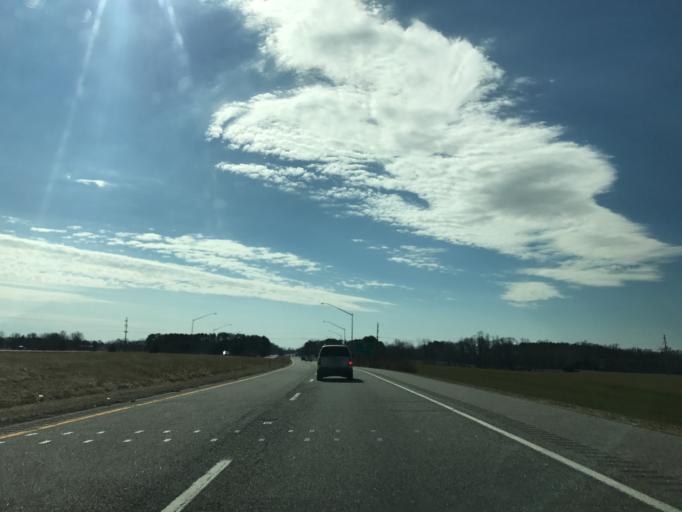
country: US
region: Delaware
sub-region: New Castle County
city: Townsend
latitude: 39.3709
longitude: -75.8137
